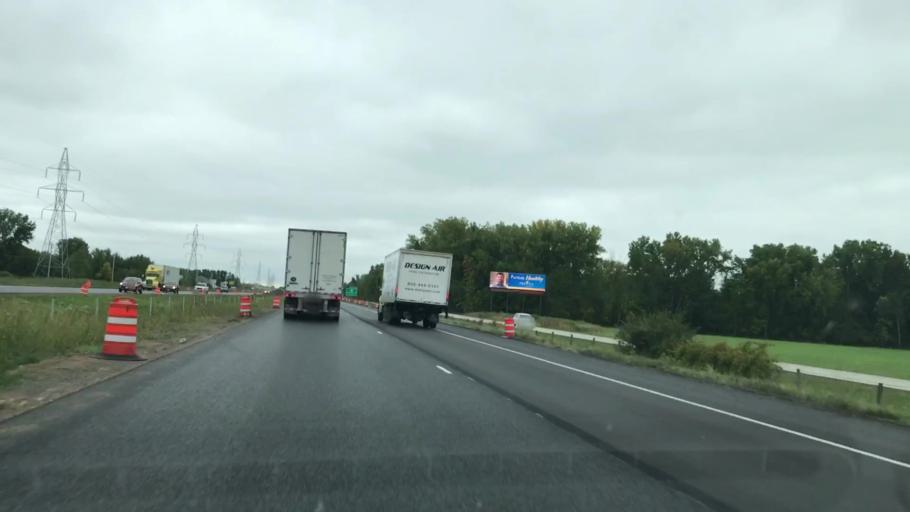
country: US
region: Wisconsin
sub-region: Brown County
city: Suamico
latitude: 44.6148
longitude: -88.0499
